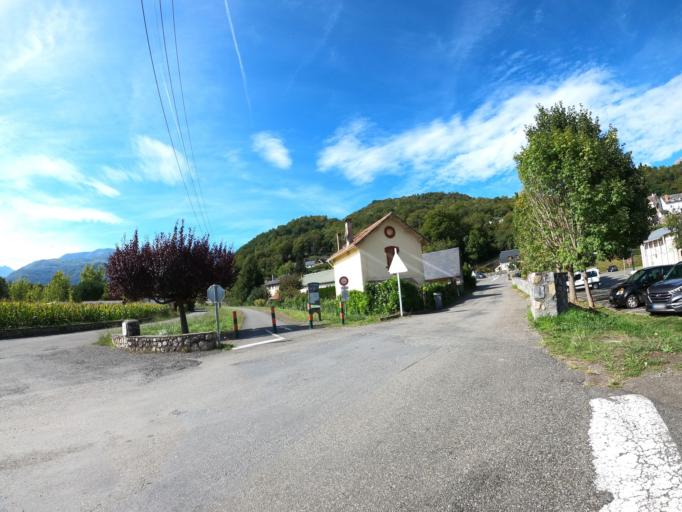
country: FR
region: Midi-Pyrenees
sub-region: Departement des Hautes-Pyrenees
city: Argeles-Gazost
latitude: 43.0193
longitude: -0.0956
